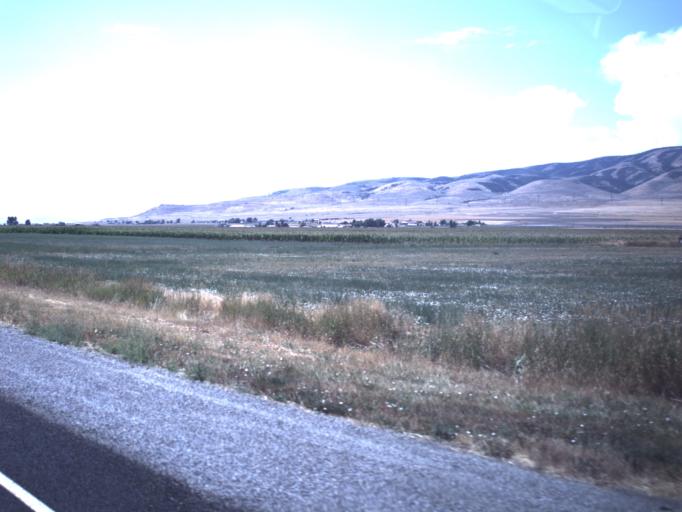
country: US
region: Utah
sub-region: Box Elder County
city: Garland
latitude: 41.8284
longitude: -112.1457
